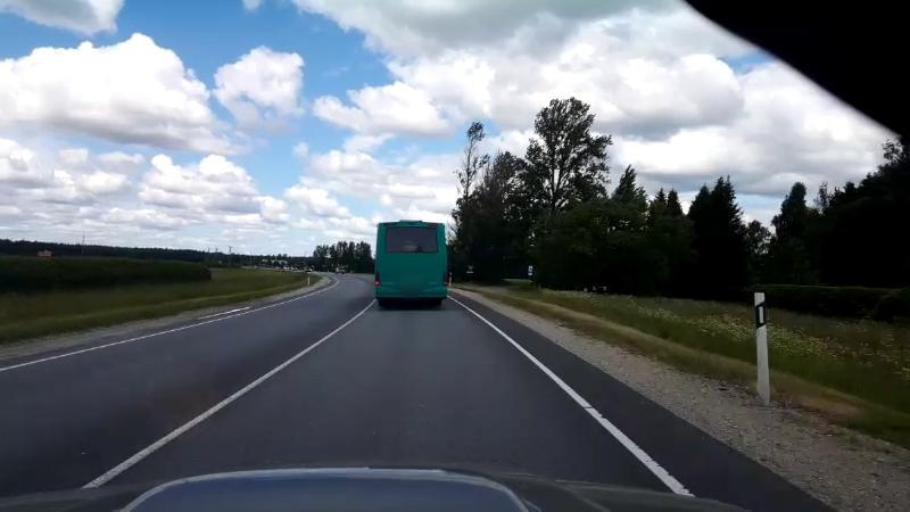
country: EE
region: Paernumaa
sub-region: Paikuse vald
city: Paikuse
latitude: 58.3066
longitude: 24.6089
